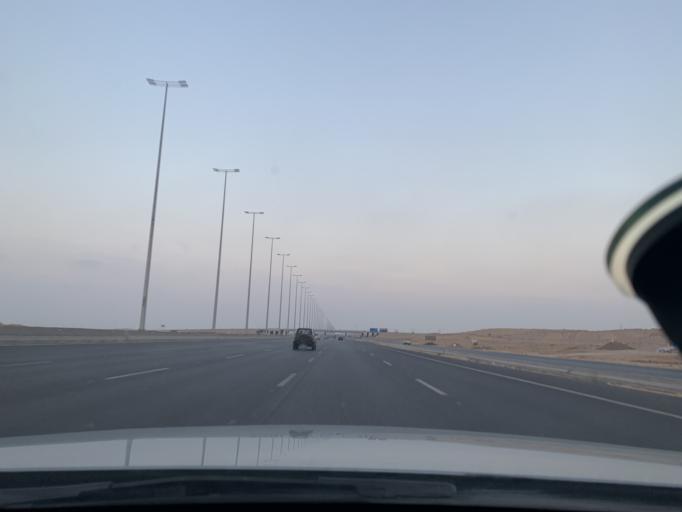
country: EG
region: Muhafazat al Qalyubiyah
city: Al Khankah
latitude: 30.0923
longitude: 31.4982
